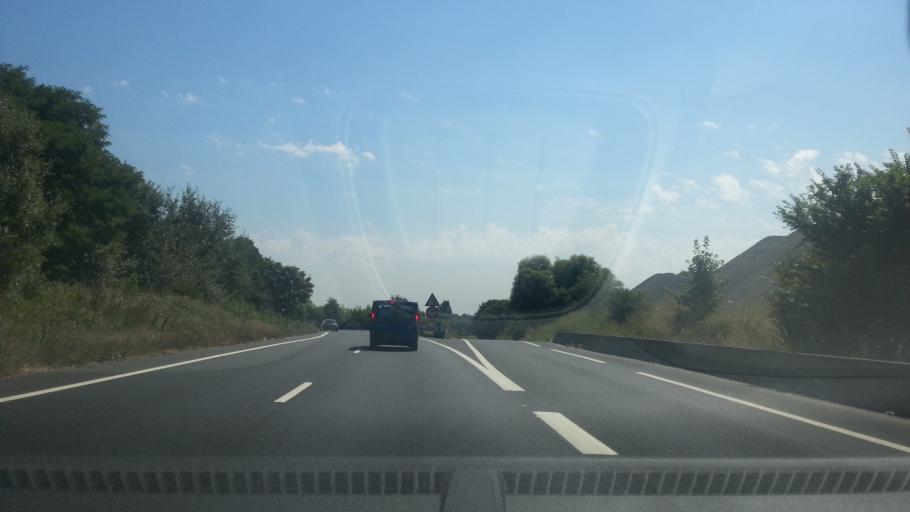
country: FR
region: Ile-de-France
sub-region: Departement de l'Essonne
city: Champlan
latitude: 48.7116
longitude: 2.2854
